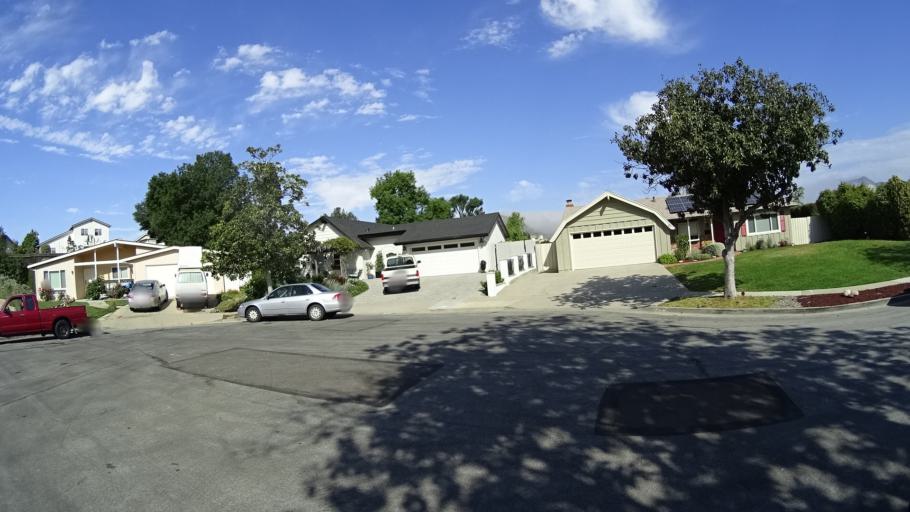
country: US
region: California
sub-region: Ventura County
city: Casa Conejo
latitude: 34.1770
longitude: -118.9432
